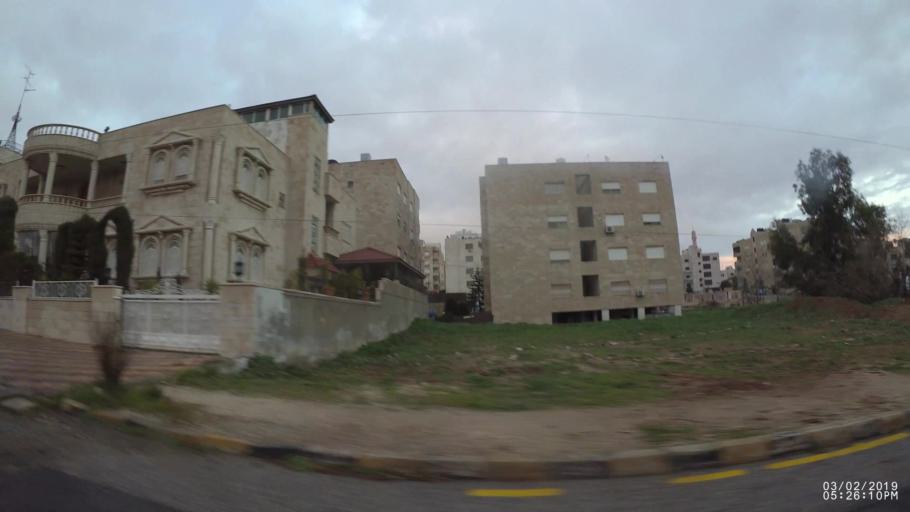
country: JO
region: Amman
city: Amman
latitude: 31.9866
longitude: 35.9103
